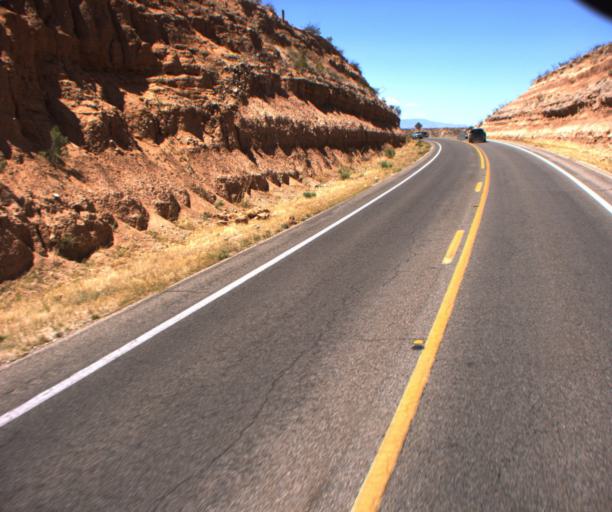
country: US
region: Arizona
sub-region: Cochise County
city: Saint David
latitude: 31.8161
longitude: -110.1665
